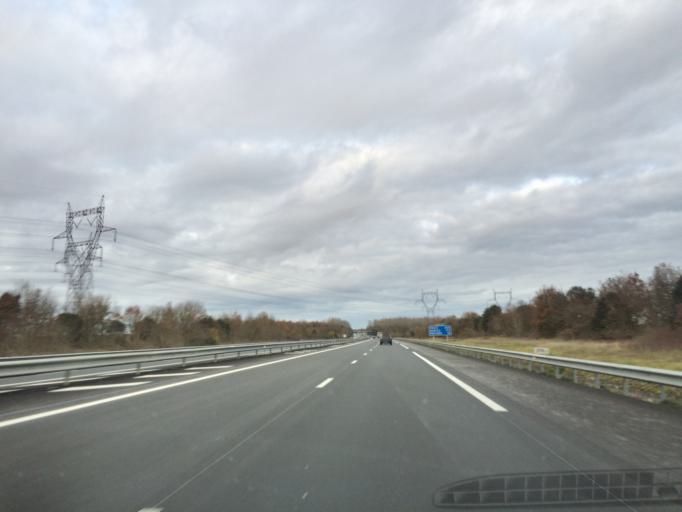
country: FR
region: Poitou-Charentes
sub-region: Departement des Deux-Sevres
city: Fors
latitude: 46.2478
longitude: -0.4272
